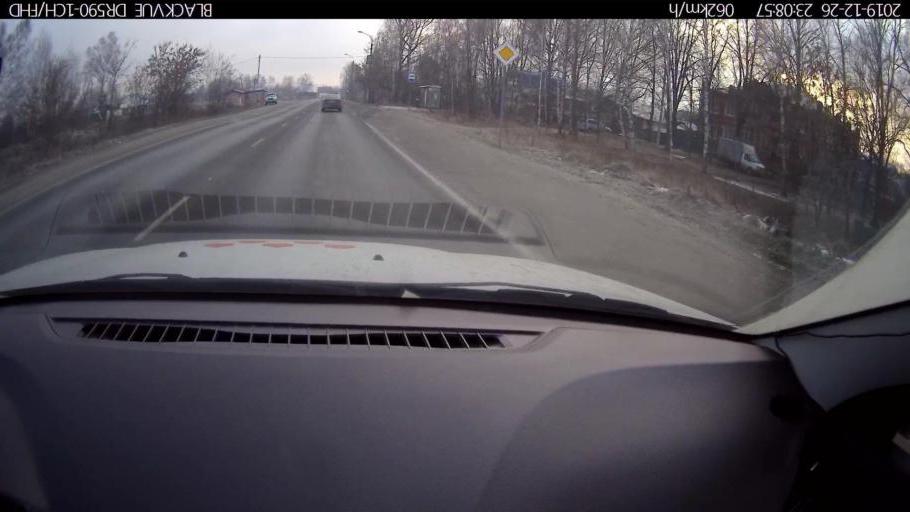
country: RU
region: Nizjnij Novgorod
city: Gorbatovka
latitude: 56.2103
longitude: 43.7660
